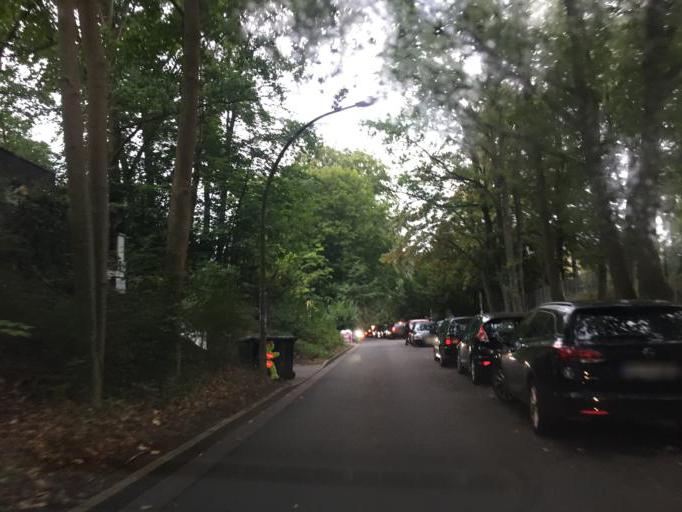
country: DE
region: Hamburg
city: Hummelsbuettel
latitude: 53.6321
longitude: 10.0470
